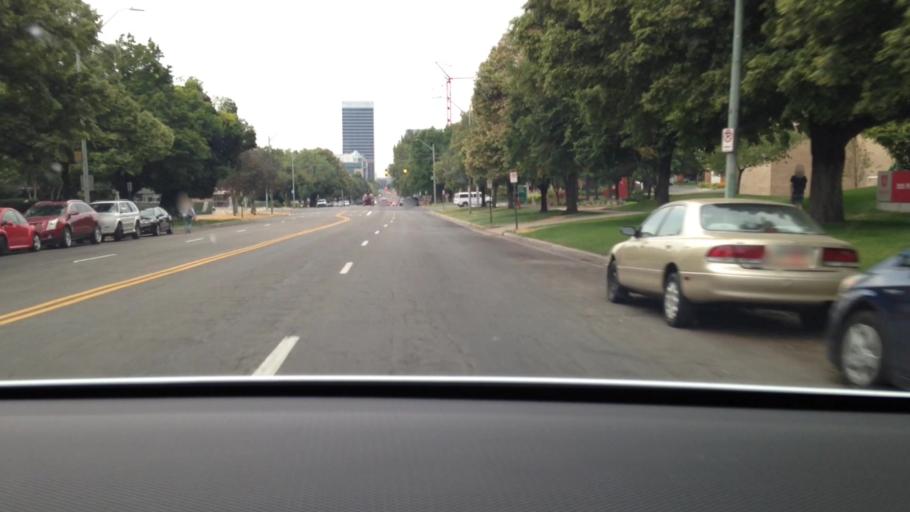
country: US
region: Utah
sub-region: Salt Lake County
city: Salt Lake City
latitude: 40.7672
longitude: -111.8751
